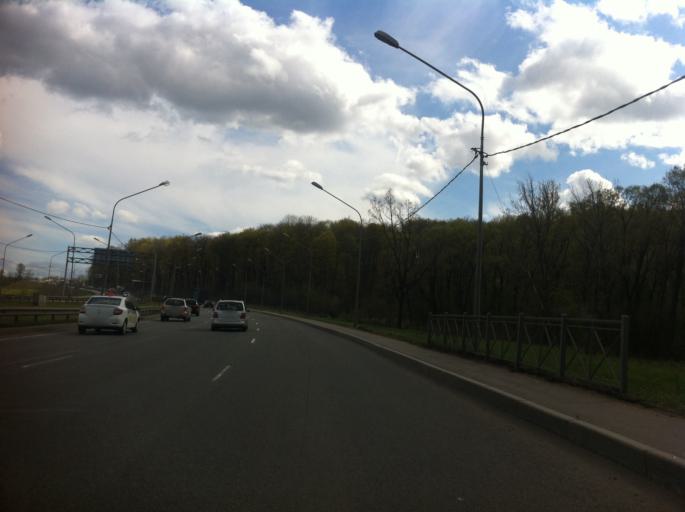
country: RU
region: St.-Petersburg
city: Aleksandrovskaya
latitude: 59.7771
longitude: 30.3253
